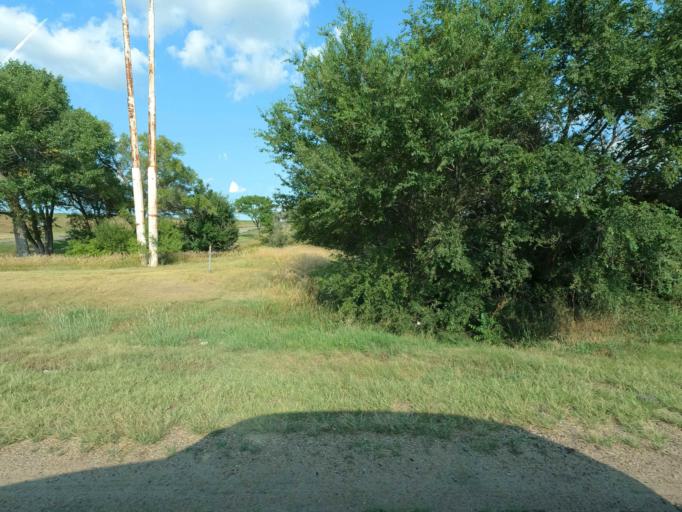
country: US
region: Kansas
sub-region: Gove County
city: Gove
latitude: 39.0567
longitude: -100.2415
